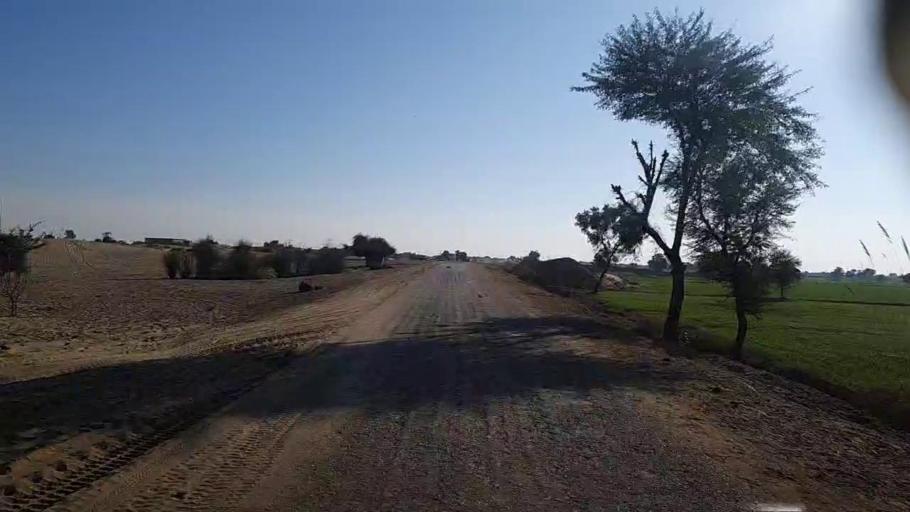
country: PK
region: Sindh
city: Khairpur
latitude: 27.9080
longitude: 69.7505
